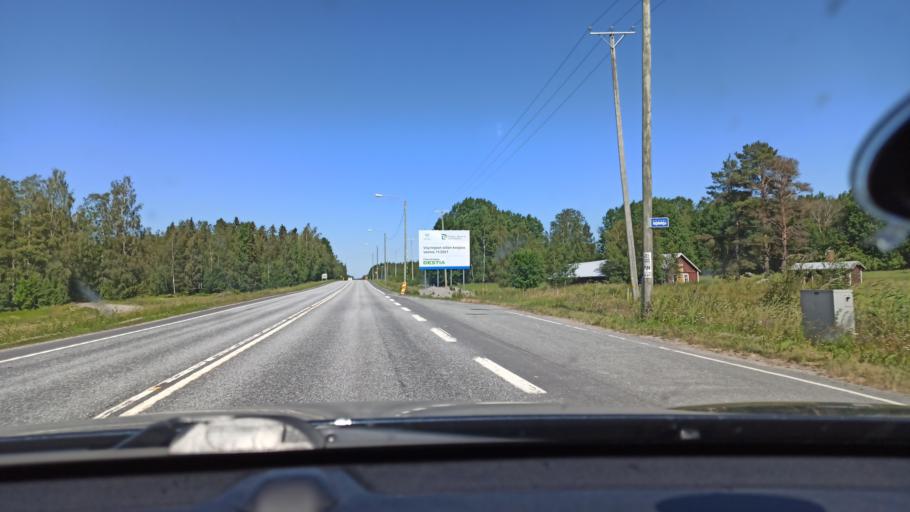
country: FI
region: Ostrobothnia
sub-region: Vaasa
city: Voera
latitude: 63.2283
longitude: 22.2391
